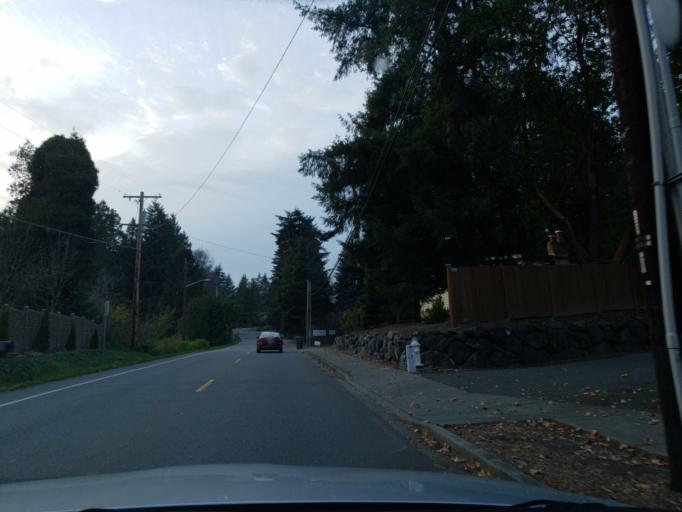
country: US
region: Washington
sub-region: King County
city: Bothell
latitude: 47.7664
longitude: -122.2128
